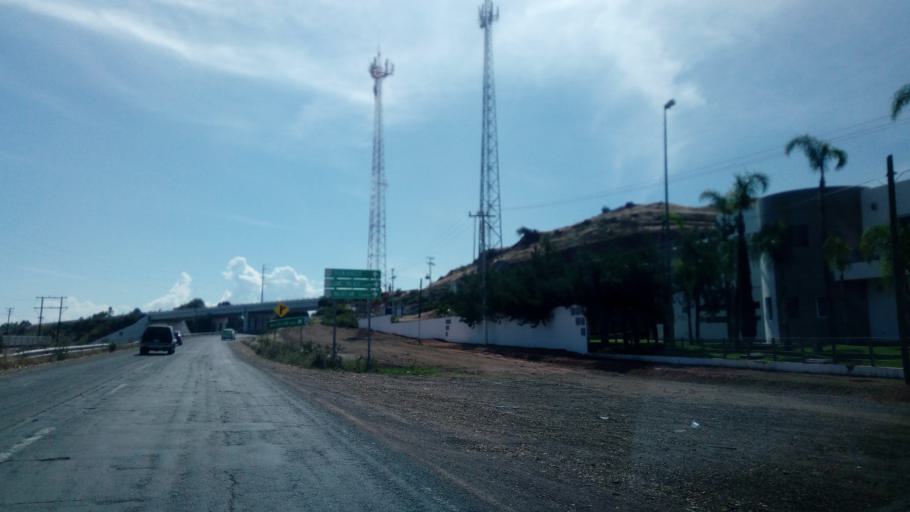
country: MX
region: Durango
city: Victoria de Durango
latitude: 24.0708
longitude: -104.6560
